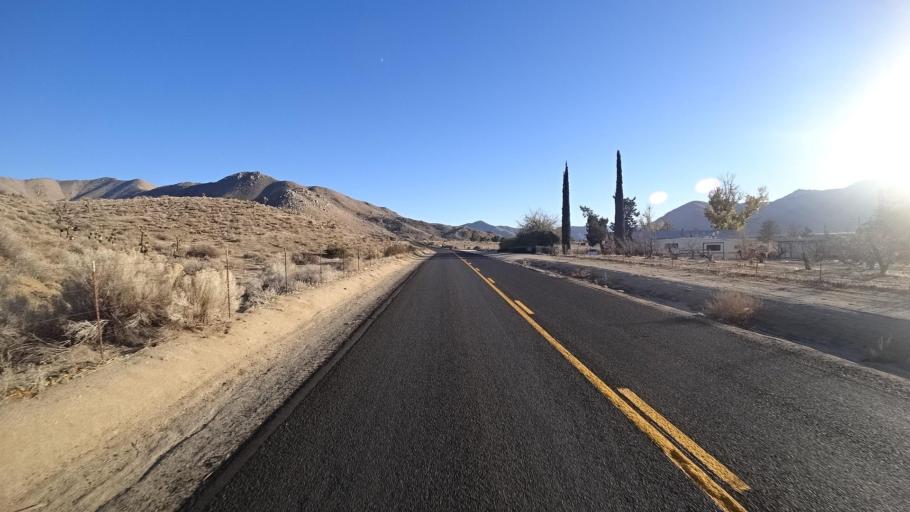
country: US
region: California
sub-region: Kern County
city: Weldon
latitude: 35.6391
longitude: -118.2479
